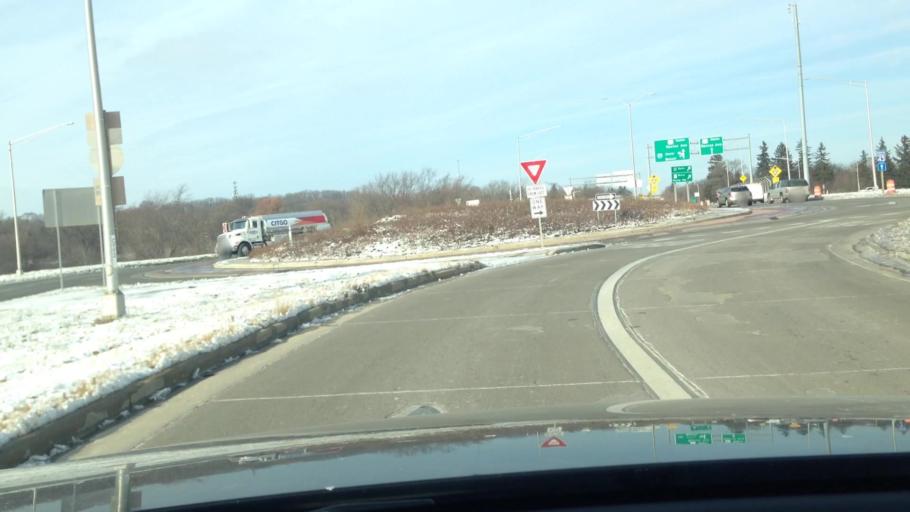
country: US
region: Wisconsin
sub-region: Waukesha County
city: Muskego
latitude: 42.9319
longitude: -88.1590
